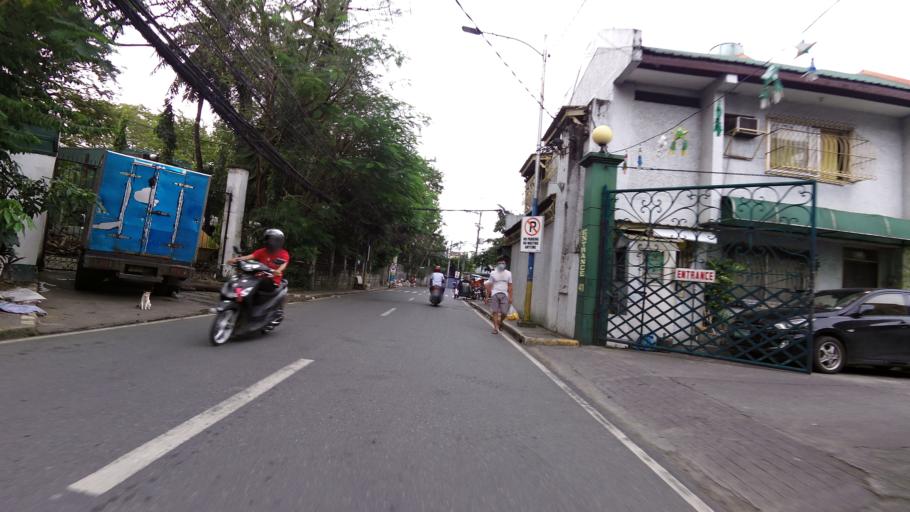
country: PH
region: Metro Manila
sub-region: Mandaluyong
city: Mandaluyong City
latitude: 14.5828
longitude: 121.0249
